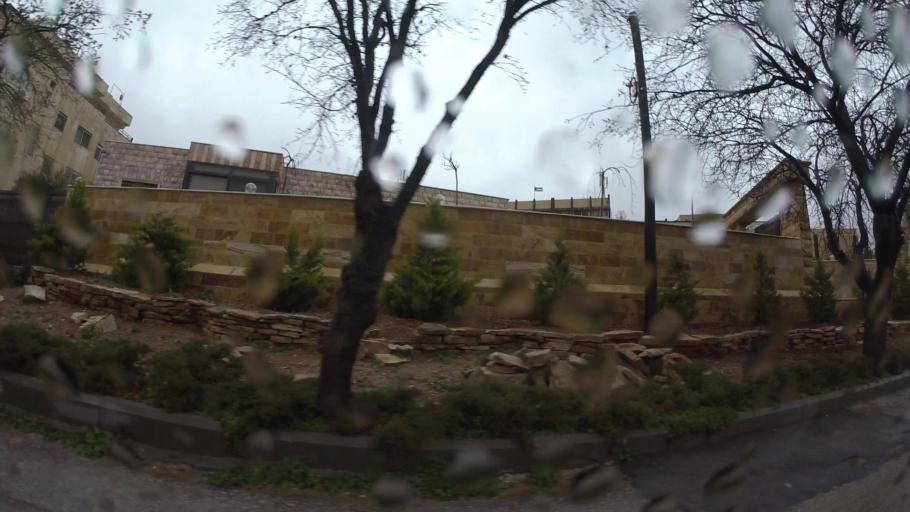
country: JO
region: Amman
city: Al Jubayhah
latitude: 32.0222
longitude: 35.8667
